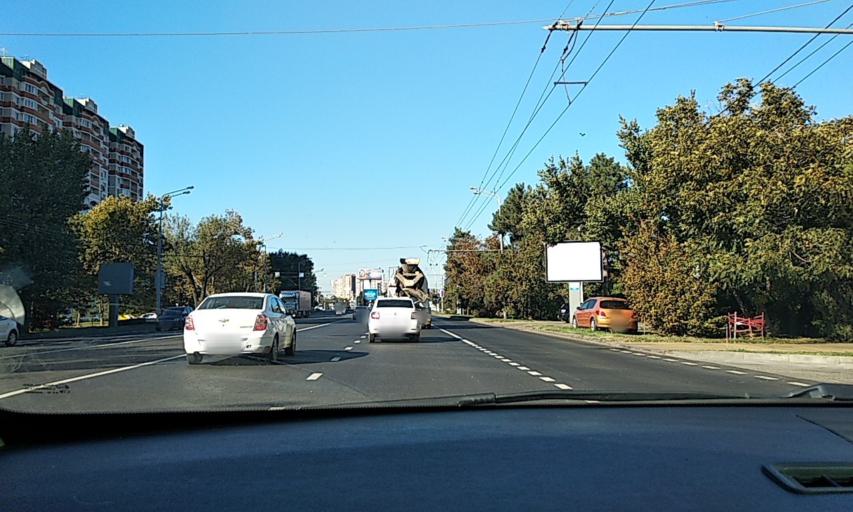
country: RU
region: Krasnodarskiy
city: Pashkovskiy
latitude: 45.0126
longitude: 39.0717
